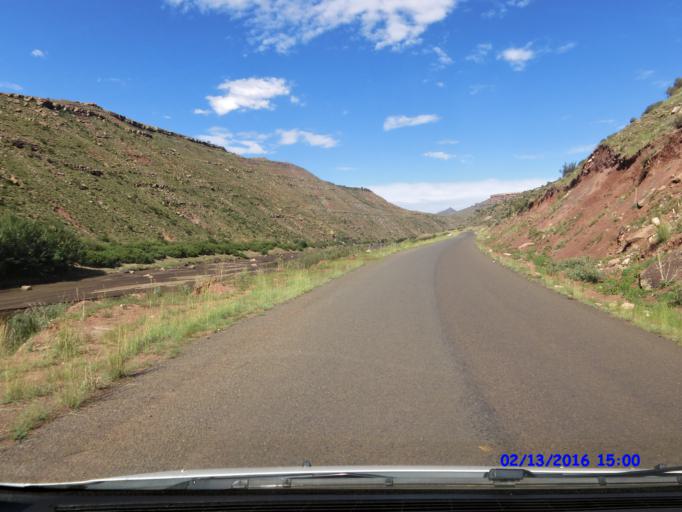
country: LS
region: Qacha's Nek
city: Qacha's Nek
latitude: -30.0661
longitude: 28.4269
